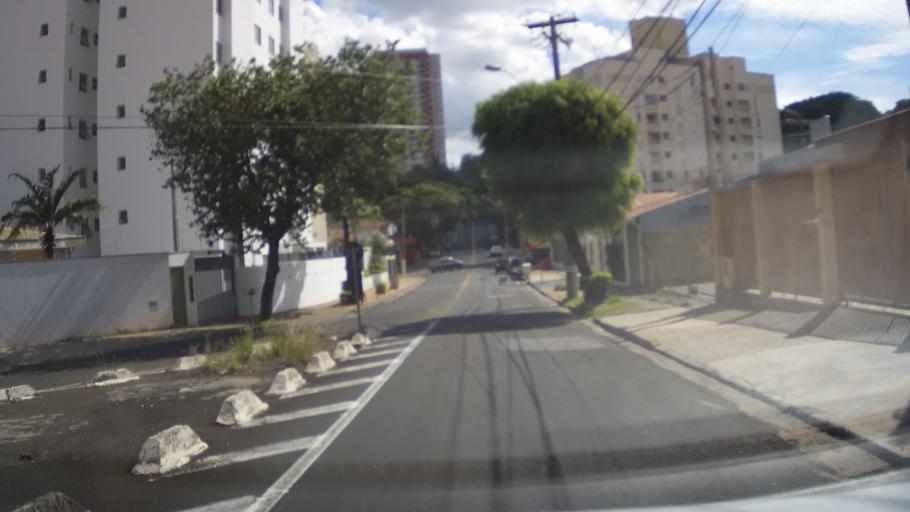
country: BR
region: Sao Paulo
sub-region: Campinas
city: Campinas
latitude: -22.9196
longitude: -47.0476
